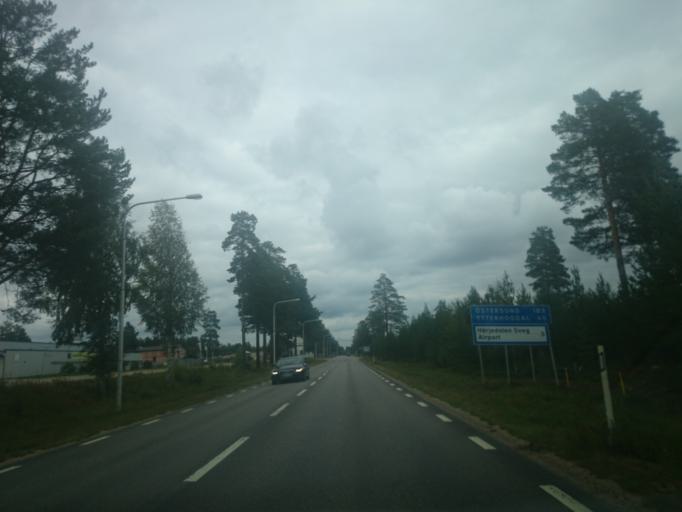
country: SE
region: Jaemtland
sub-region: Harjedalens Kommun
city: Sveg
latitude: 62.0358
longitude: 14.3801
